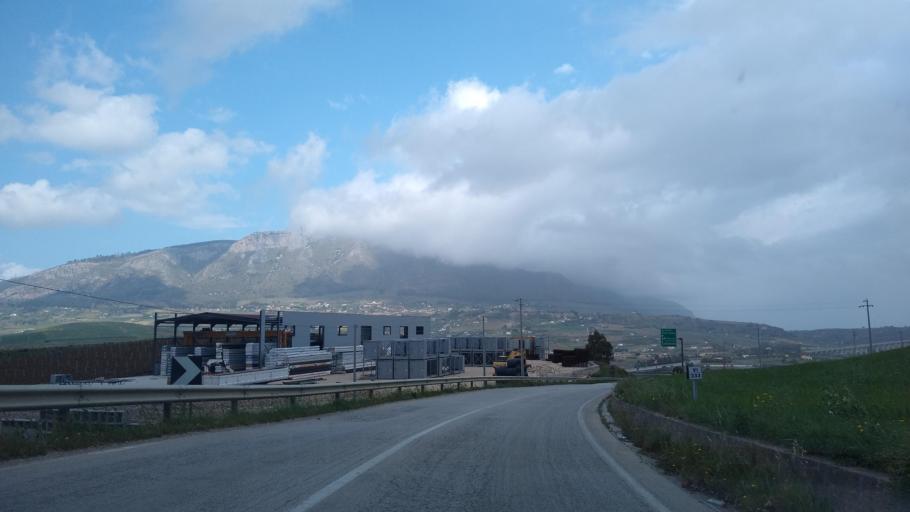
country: IT
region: Sicily
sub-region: Trapani
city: Alcamo
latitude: 37.9708
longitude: 12.9291
